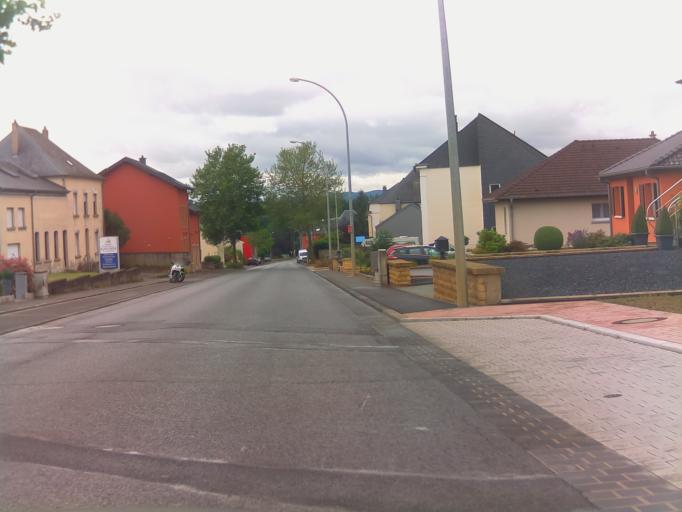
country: LU
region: Luxembourg
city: Aspelt
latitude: 49.5234
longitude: 6.2294
